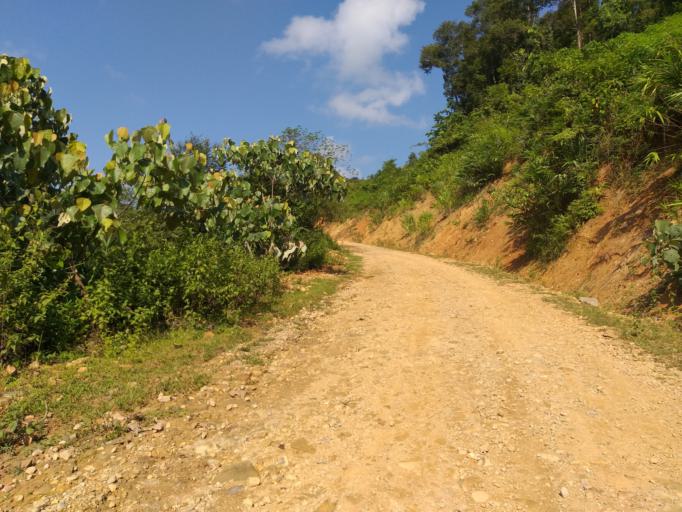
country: LA
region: Phongsali
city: Khoa
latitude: 21.2109
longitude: 102.6113
